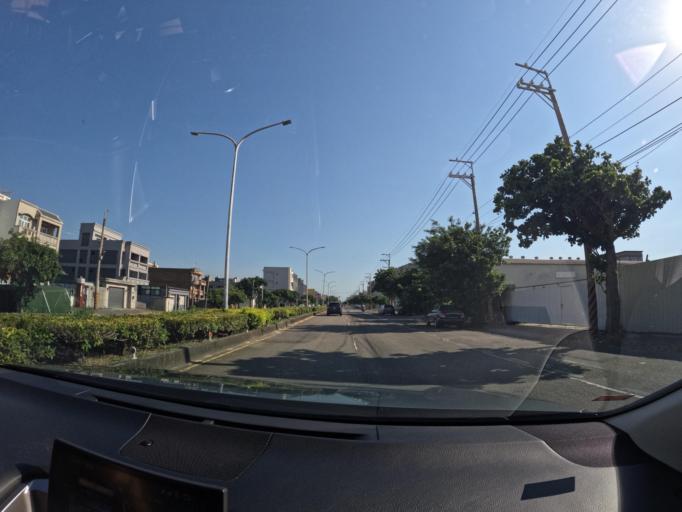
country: TW
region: Taiwan
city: Fengyuan
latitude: 24.2564
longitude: 120.5522
